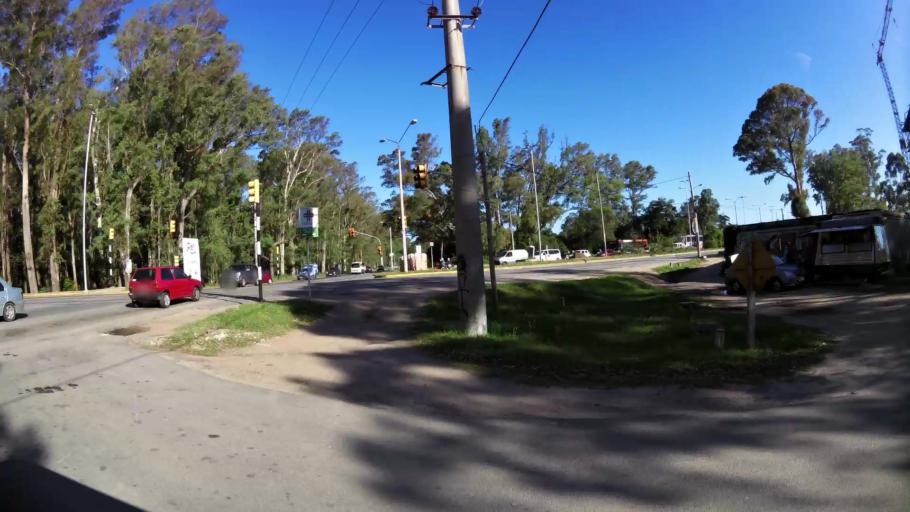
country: UY
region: Canelones
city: Barra de Carrasco
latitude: -34.8593
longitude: -56.0303
